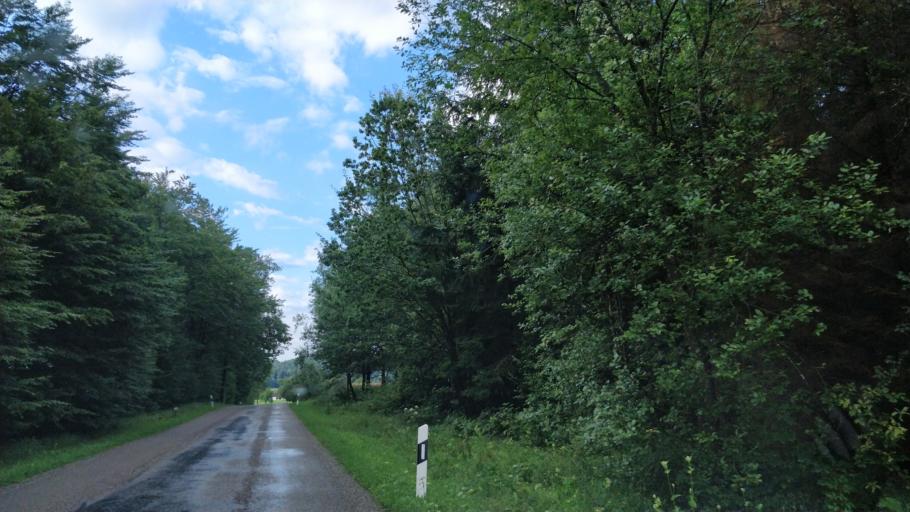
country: DE
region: Baden-Wuerttemberg
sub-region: Regierungsbezirk Stuttgart
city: Fichtenberg
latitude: 48.9631
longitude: 9.6784
